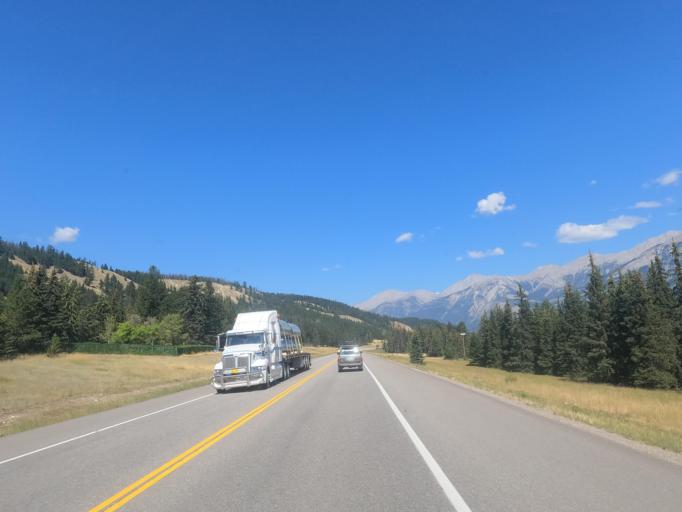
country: CA
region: Alberta
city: Jasper Park Lodge
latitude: 52.9000
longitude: -118.0661
